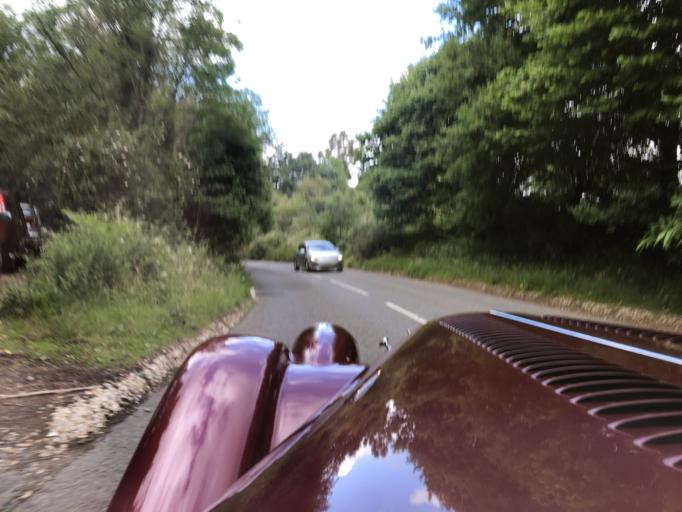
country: GB
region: England
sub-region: East Sussex
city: Wadhurst
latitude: 51.0862
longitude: 0.4016
